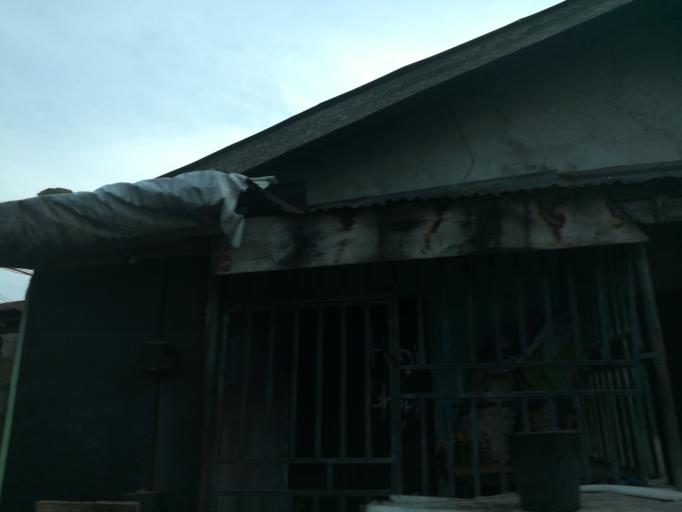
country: NG
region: Rivers
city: Port Harcourt
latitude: 4.8136
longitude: 7.0235
